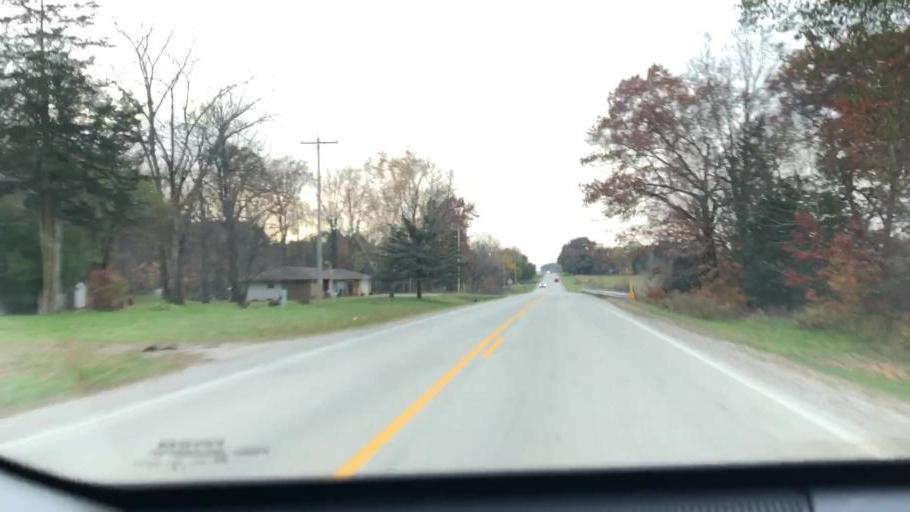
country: US
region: Wisconsin
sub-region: Brown County
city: Oneida
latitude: 44.4443
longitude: -88.2390
